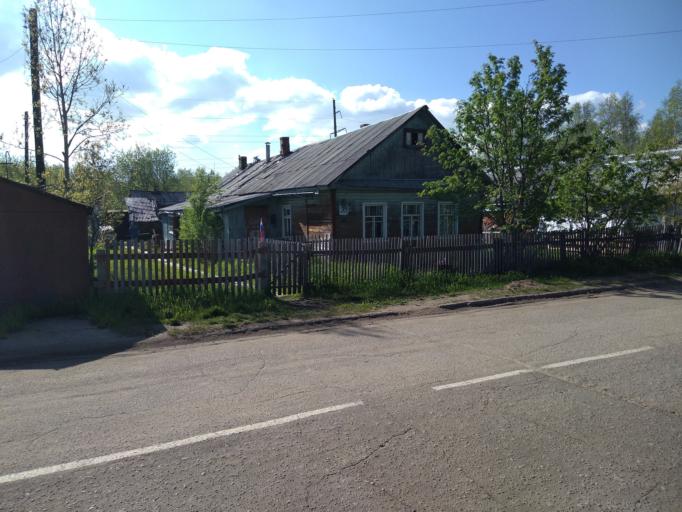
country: RU
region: Komi Republic
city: Puteyets
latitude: 65.1168
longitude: 57.1480
